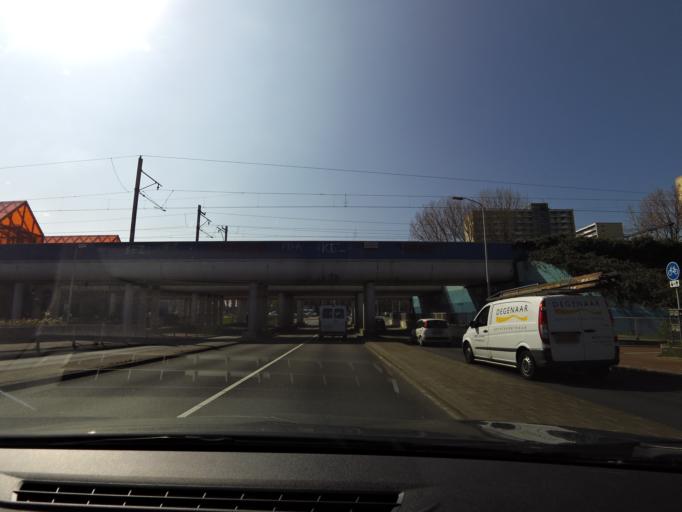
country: NL
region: South Holland
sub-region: Gemeente Den Haag
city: The Hague
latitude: 52.0550
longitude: 4.3093
